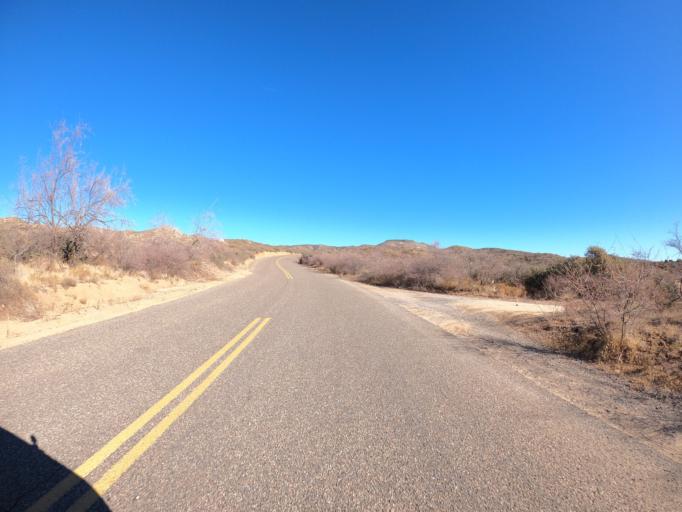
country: US
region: Arizona
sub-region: Yavapai County
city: Dewey-Humboldt
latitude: 34.5431
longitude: -112.0804
